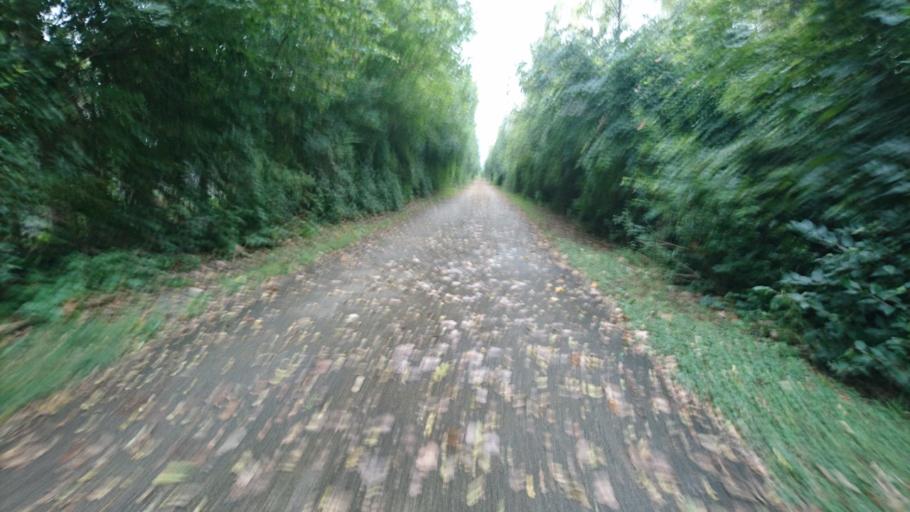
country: US
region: Illinois
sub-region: Sangamon County
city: Southern View
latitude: 39.7330
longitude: -89.6725
